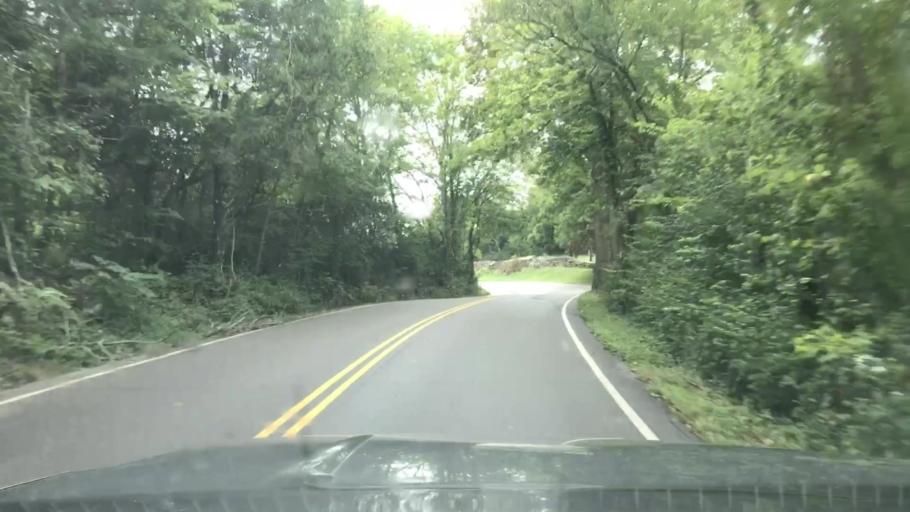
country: US
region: Tennessee
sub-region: Davidson County
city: Forest Hills
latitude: 36.0392
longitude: -86.8556
